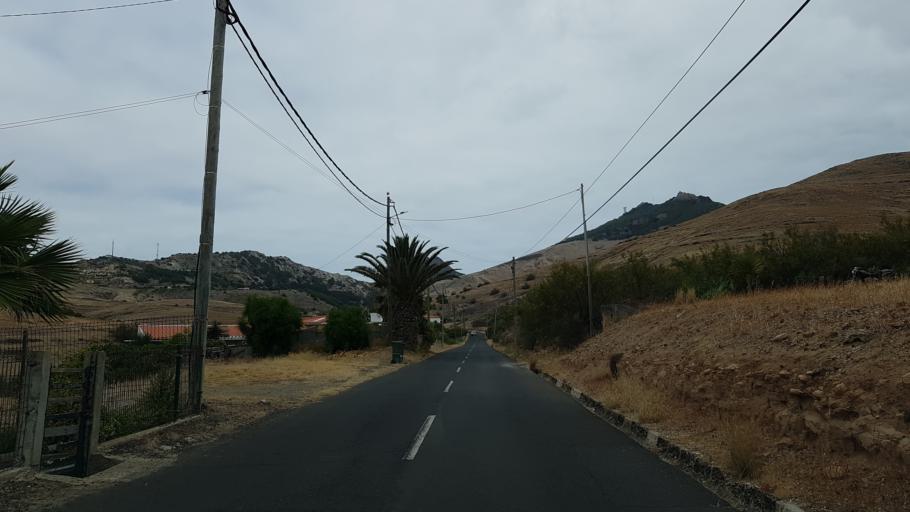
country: PT
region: Madeira
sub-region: Porto Santo
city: Vila de Porto Santo
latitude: 33.0715
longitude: -16.3028
